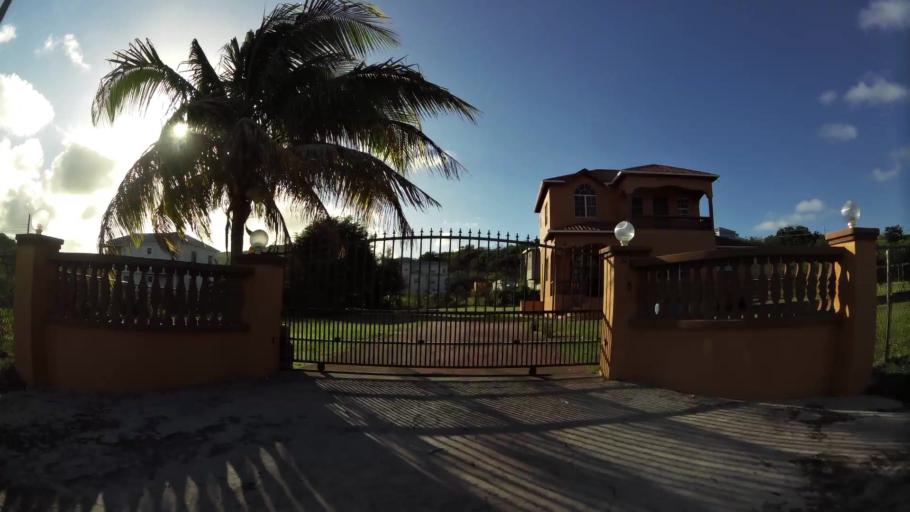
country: AG
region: Saint George
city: Piggotts
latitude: 17.1278
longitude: -61.7933
